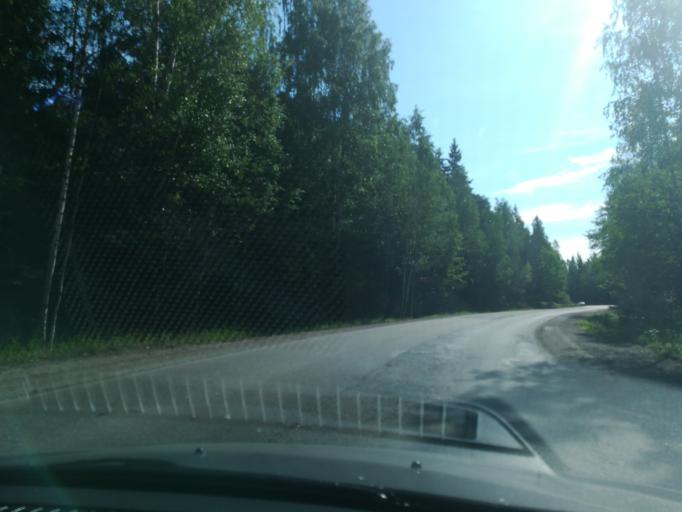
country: RU
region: Leningrad
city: Lesogorskiy
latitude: 60.9010
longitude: 28.8538
